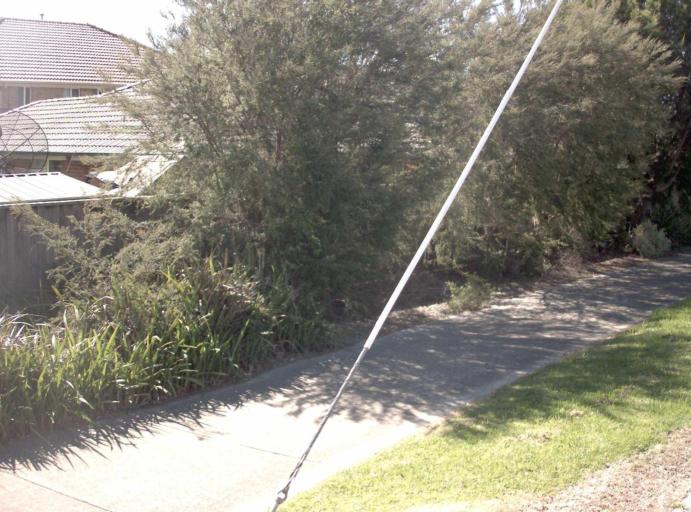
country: AU
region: Victoria
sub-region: Knox
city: Knoxfield
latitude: -37.8715
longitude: 145.2601
